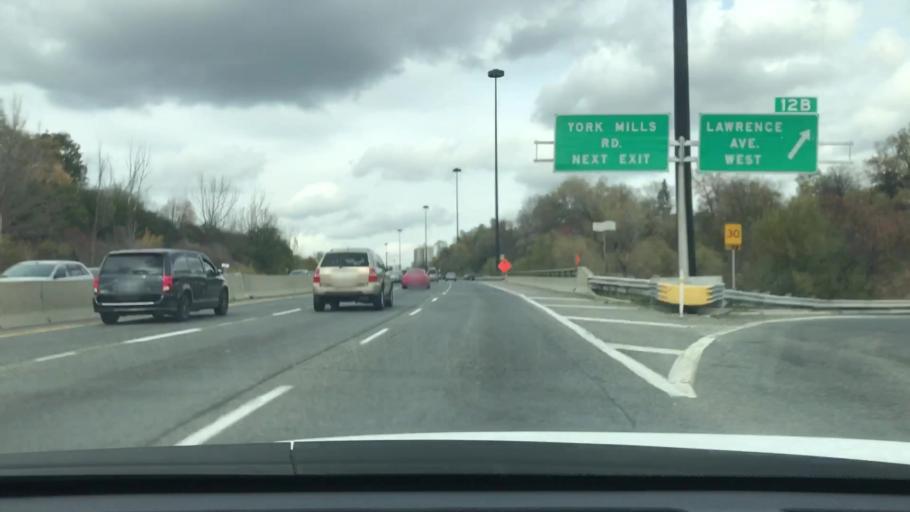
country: CA
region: Ontario
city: Willowdale
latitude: 43.7410
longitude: -79.3320
